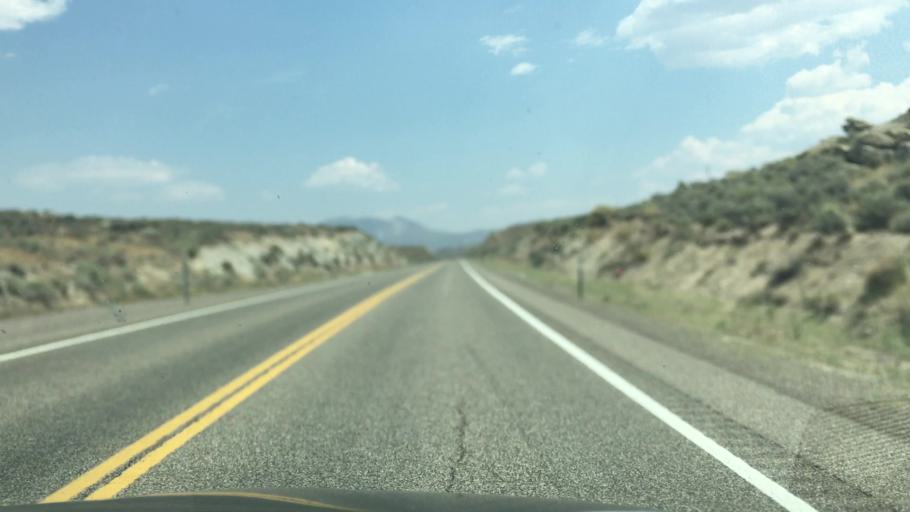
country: US
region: Nevada
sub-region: Elko County
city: Jackpot
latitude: 41.7377
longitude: -114.7855
